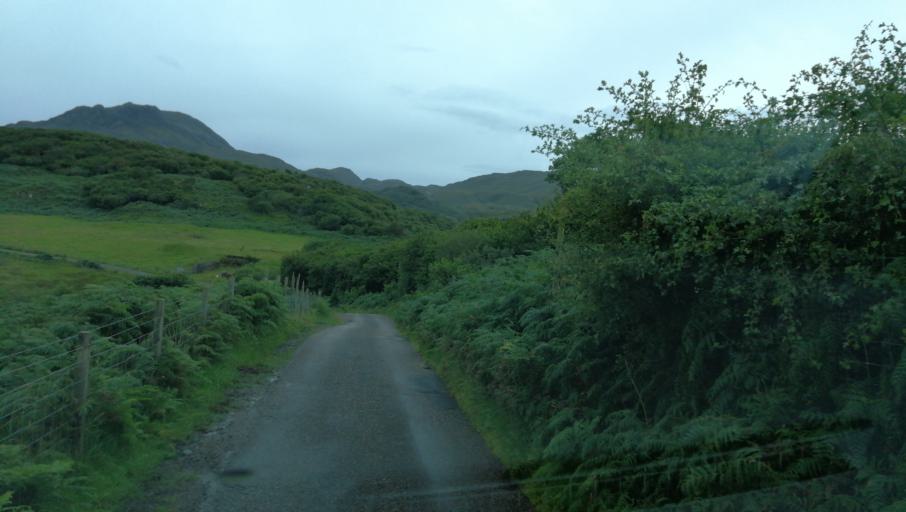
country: GB
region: Scotland
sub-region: Argyll and Bute
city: Isle Of Mull
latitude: 56.7248
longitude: -6.1776
